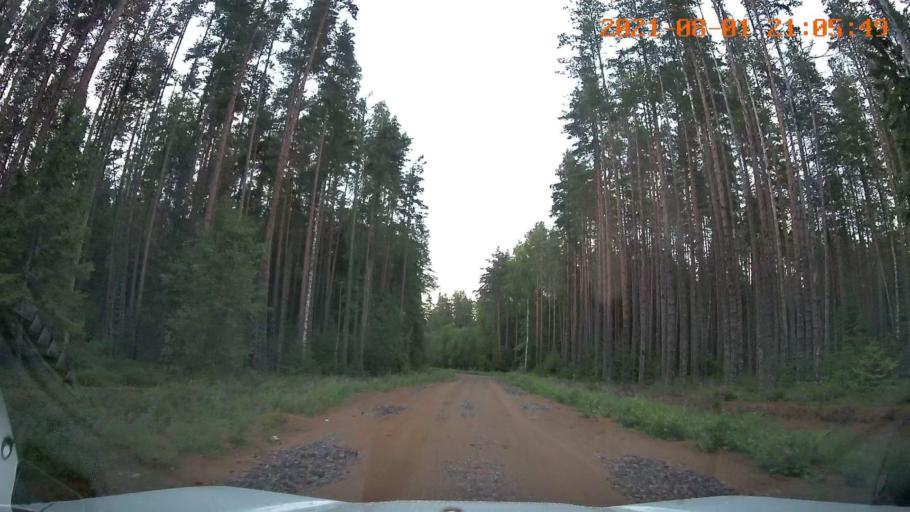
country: RU
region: Leningrad
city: Syas'stroy
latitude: 60.4996
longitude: 32.6506
